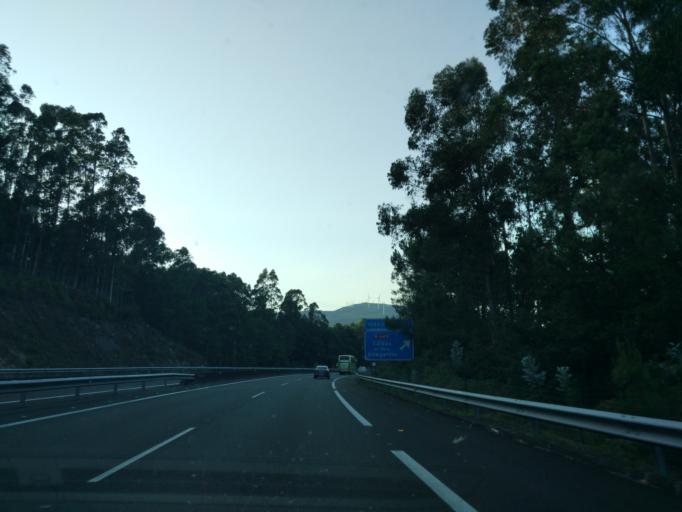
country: ES
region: Galicia
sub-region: Provincia de Pontevedra
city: Portas
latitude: 42.5909
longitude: -8.6769
